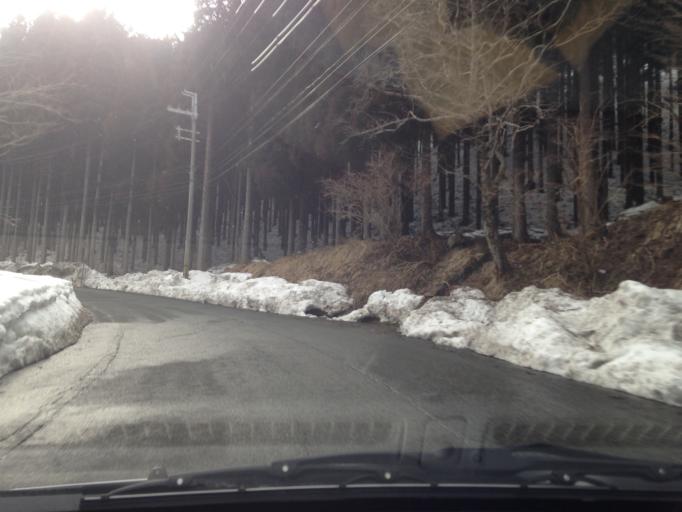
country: JP
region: Hyogo
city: Yamazakicho-nakabirose
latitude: 35.2072
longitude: 134.4043
